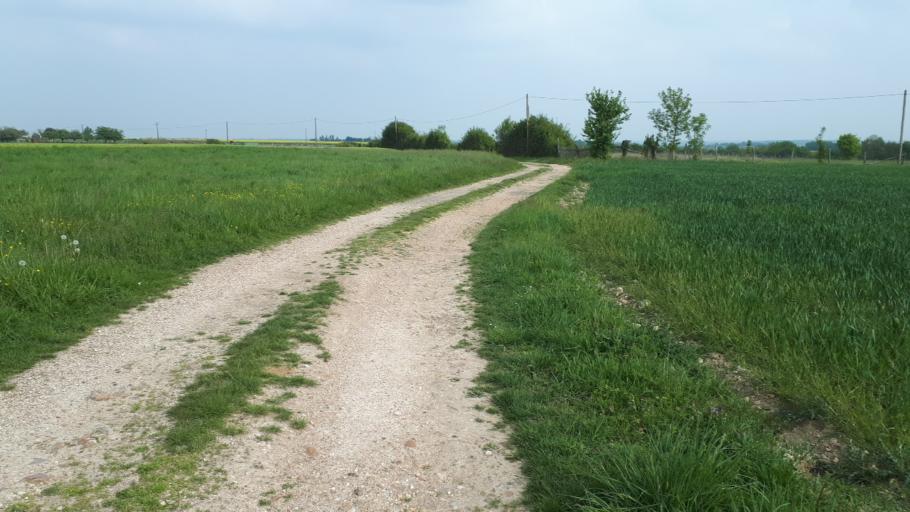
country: FR
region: Centre
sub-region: Departement du Loir-et-Cher
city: Lunay
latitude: 47.8341
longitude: 0.9416
